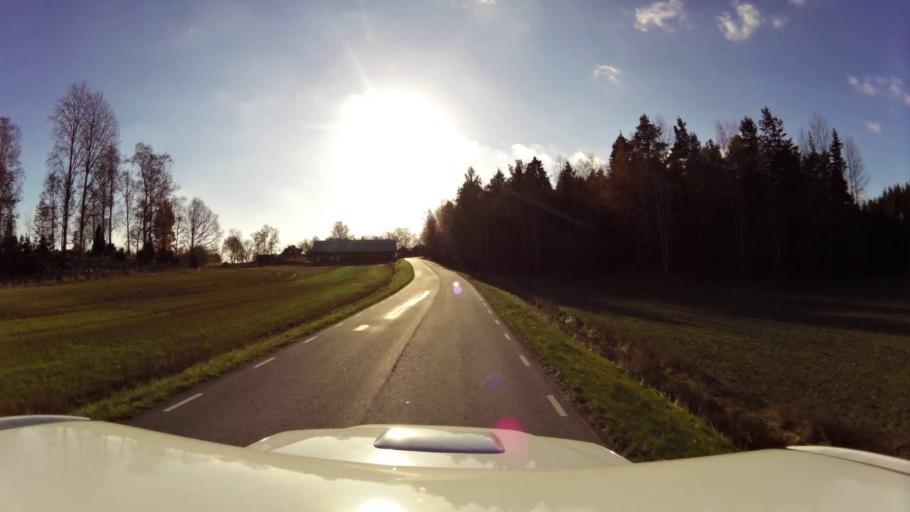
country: SE
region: OEstergoetland
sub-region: Linkopings Kommun
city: Linghem
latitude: 58.4458
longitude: 15.7827
